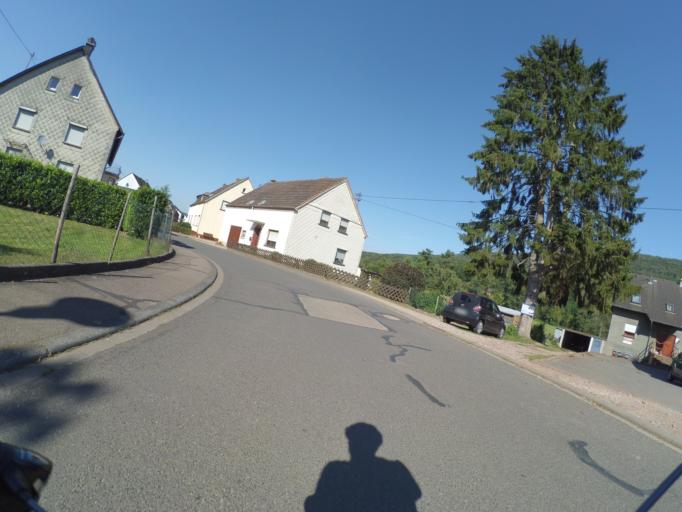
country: DE
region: Rheinland-Pfalz
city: Rivenich
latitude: 49.8732
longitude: 6.8462
